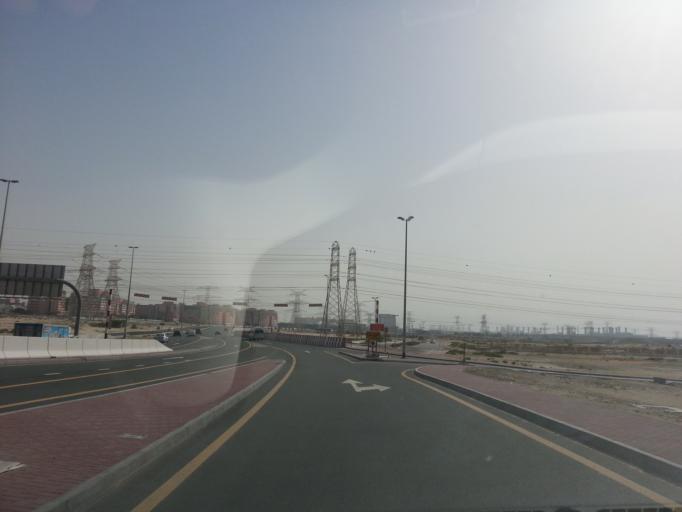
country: AE
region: Dubai
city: Dubai
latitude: 25.0568
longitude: 55.1374
